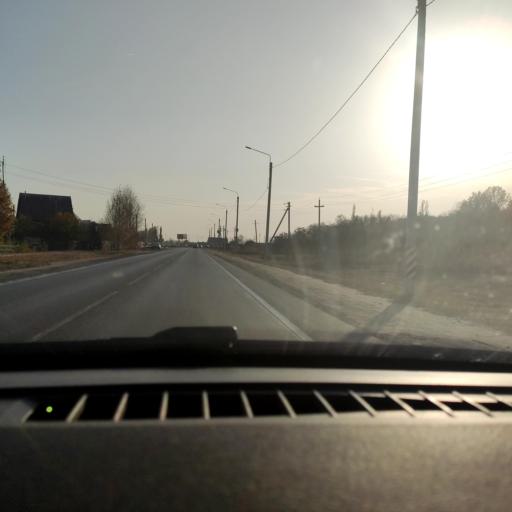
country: RU
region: Voronezj
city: Semiluki
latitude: 51.7284
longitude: 39.0373
